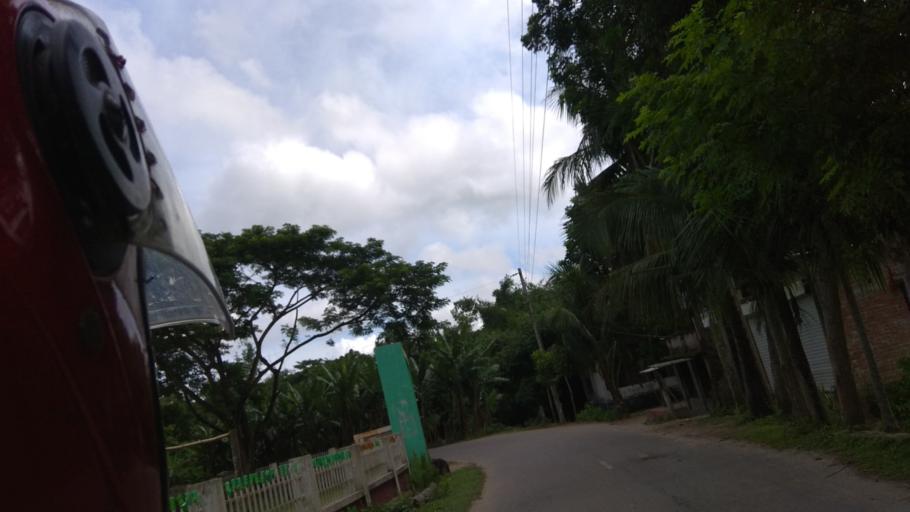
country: BD
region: Khulna
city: Kalia
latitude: 23.1380
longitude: 89.6448
